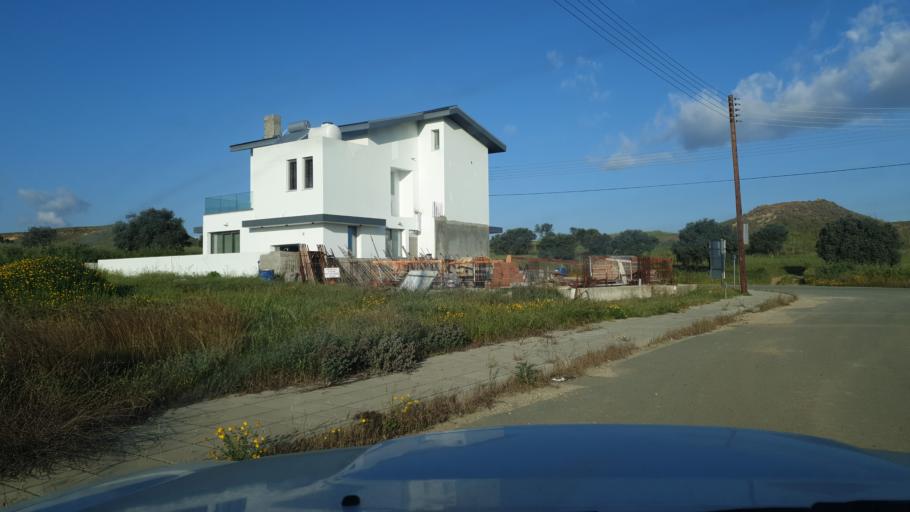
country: CY
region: Lefkosia
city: Tseri
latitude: 35.0650
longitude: 33.3186
